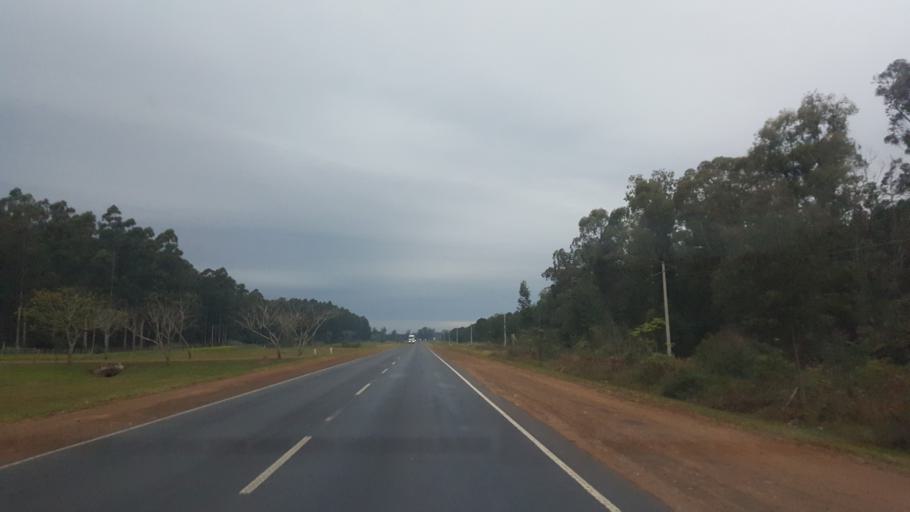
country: AR
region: Corrientes
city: Ituzaingo
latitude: -27.6092
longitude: -56.4380
